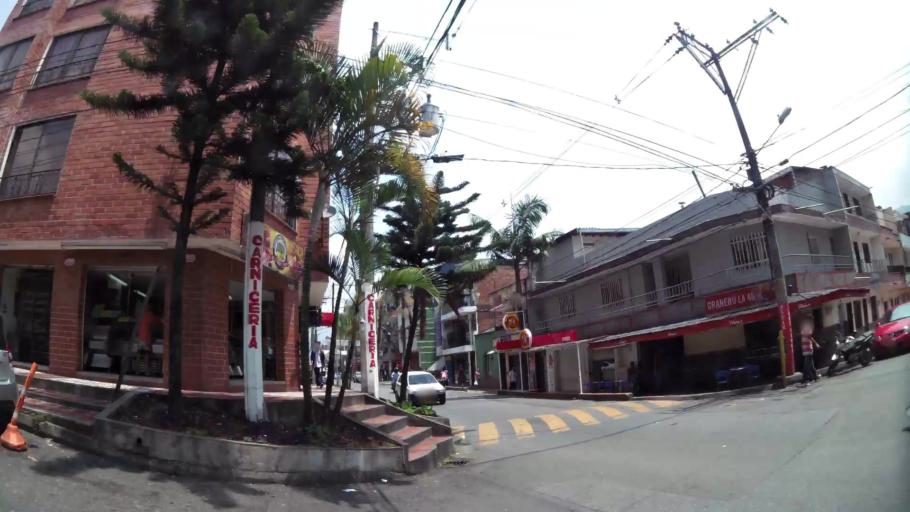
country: CO
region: Antioquia
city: Sabaneta
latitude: 6.1686
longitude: -75.6127
